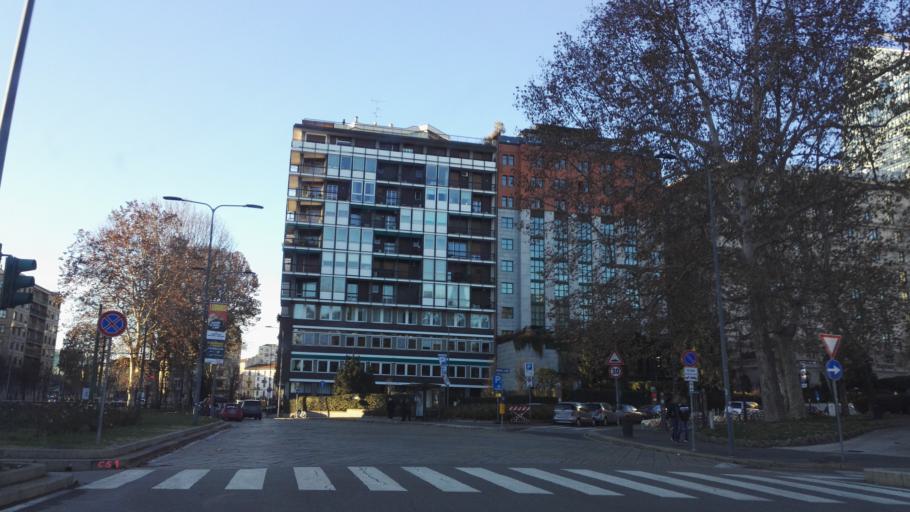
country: IT
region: Lombardy
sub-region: Citta metropolitana di Milano
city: Milano
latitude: 45.4786
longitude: 9.1969
